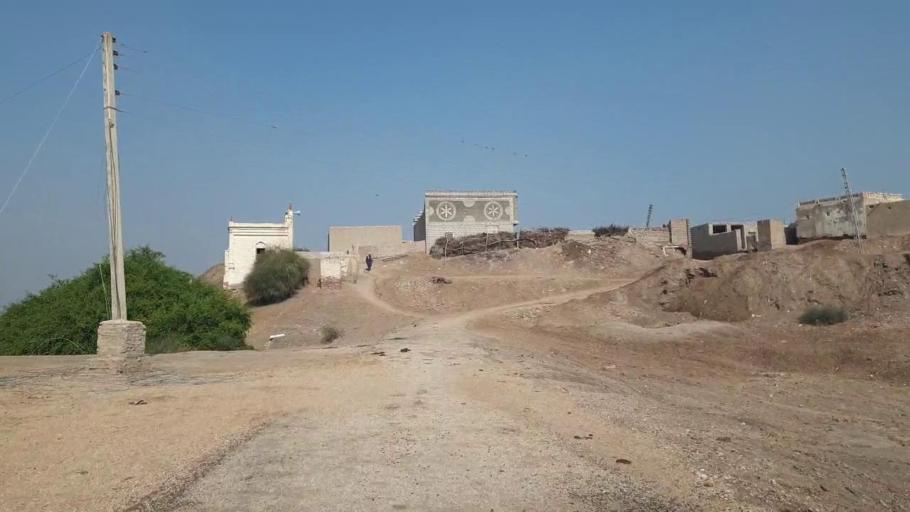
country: PK
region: Sindh
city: Sehwan
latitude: 26.4278
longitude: 67.7960
